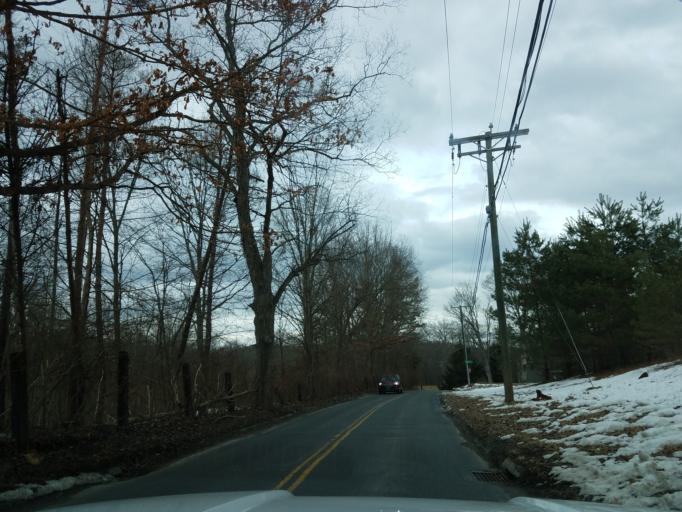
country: US
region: Connecticut
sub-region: Litchfield County
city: New Milford
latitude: 41.6024
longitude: -73.4276
